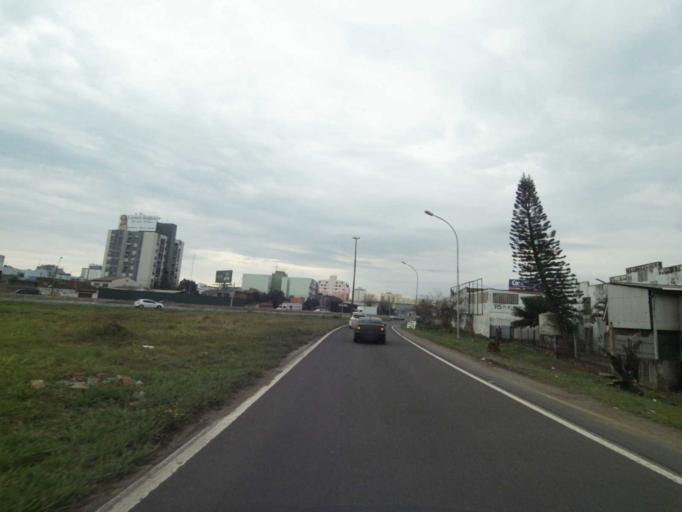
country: BR
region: Rio Grande do Sul
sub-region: Sao Leopoldo
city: Sao Leopoldo
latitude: -29.7620
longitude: -51.1534
